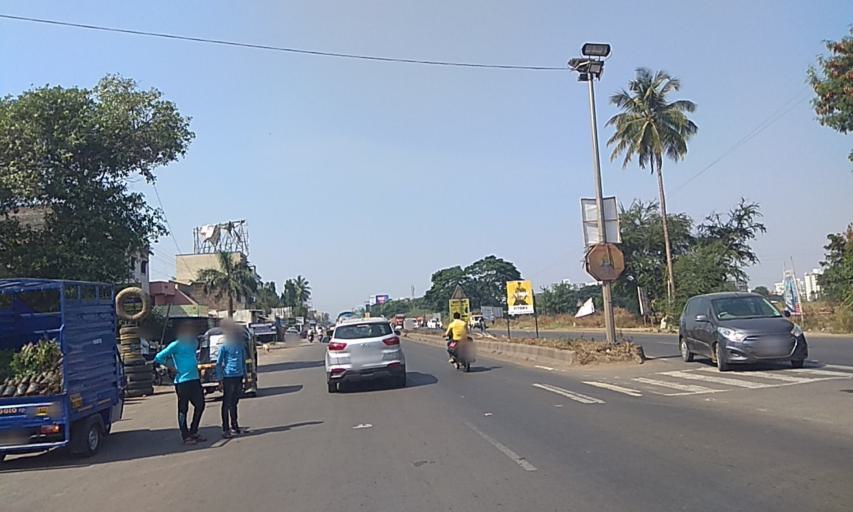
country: IN
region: Maharashtra
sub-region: Pune Division
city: Lohogaon
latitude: 18.4955
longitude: 73.9764
